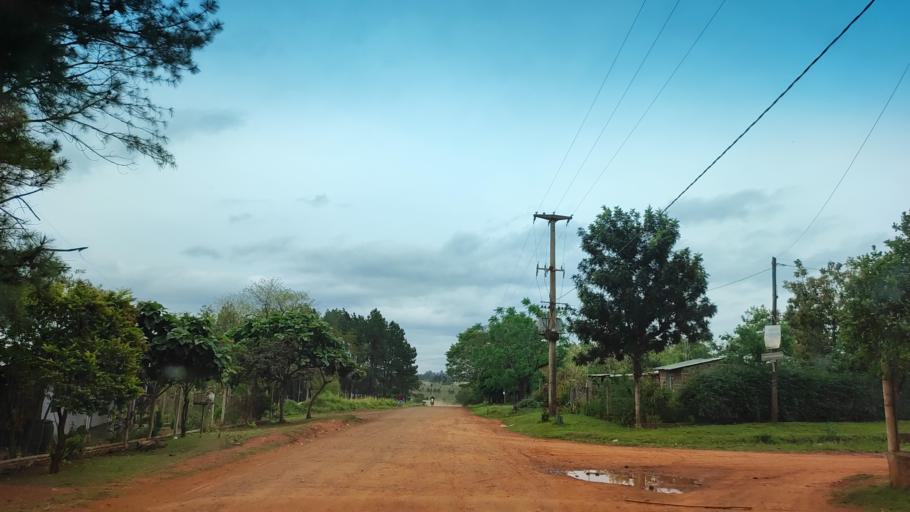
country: AR
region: Misiones
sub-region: Departamento de Capital
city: Posadas
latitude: -27.4687
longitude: -55.9628
